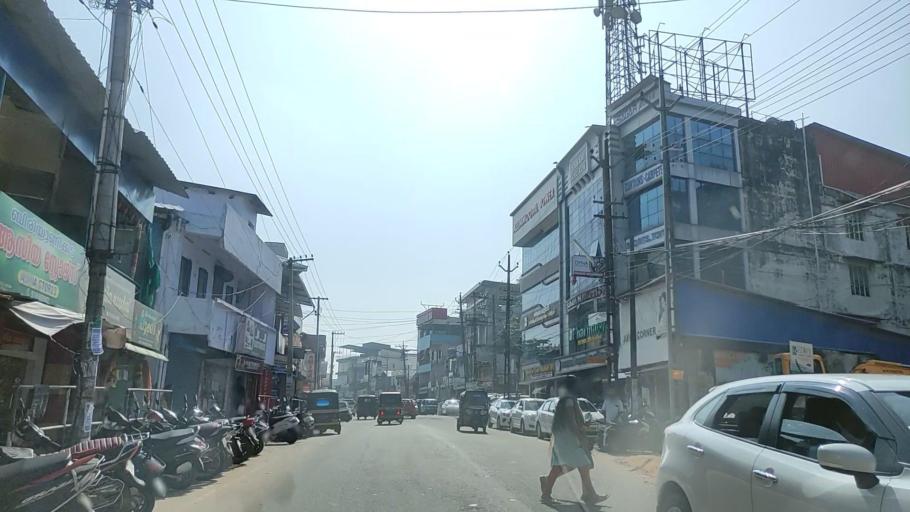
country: IN
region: Kerala
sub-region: Kollam
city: Punalur
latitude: 8.9272
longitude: 76.9149
